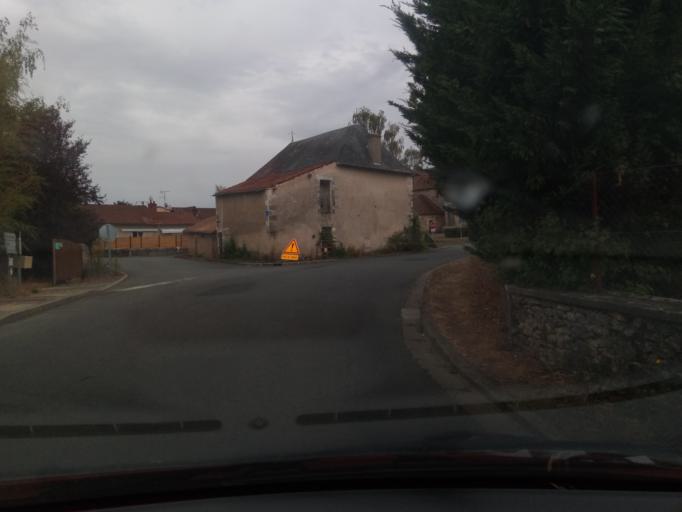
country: FR
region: Poitou-Charentes
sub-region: Departement de la Vienne
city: Saint-Savin
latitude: 46.5793
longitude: 0.7770
